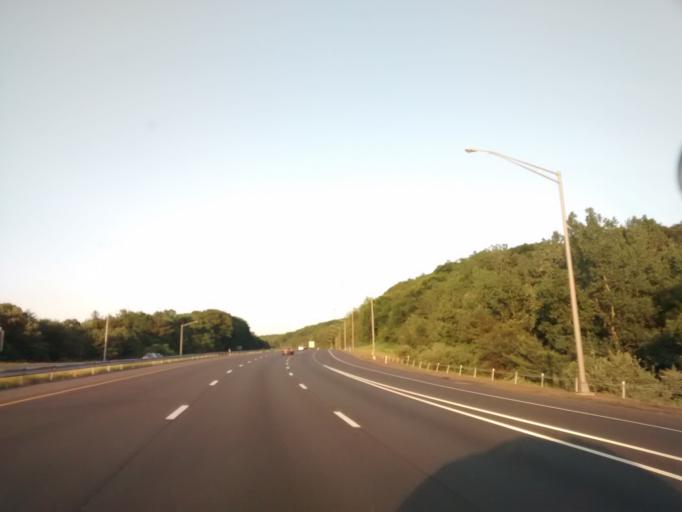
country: US
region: Connecticut
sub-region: Tolland County
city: Rockville
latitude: 41.8550
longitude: -72.4250
